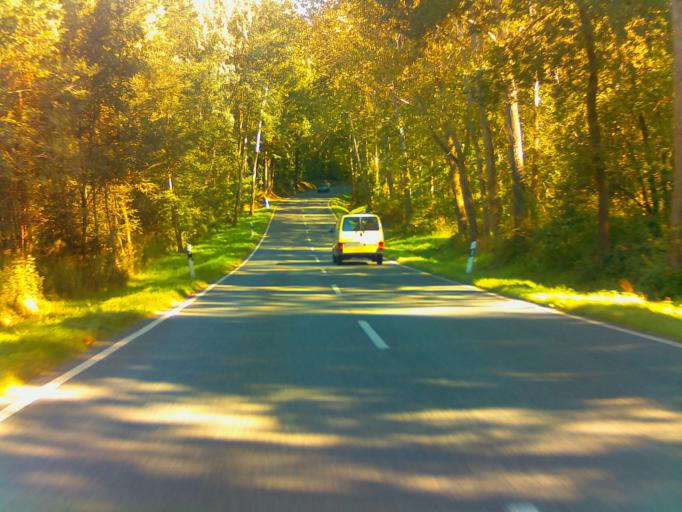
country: DE
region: Thuringia
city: Tautendorf
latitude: 50.8115
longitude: 11.9110
